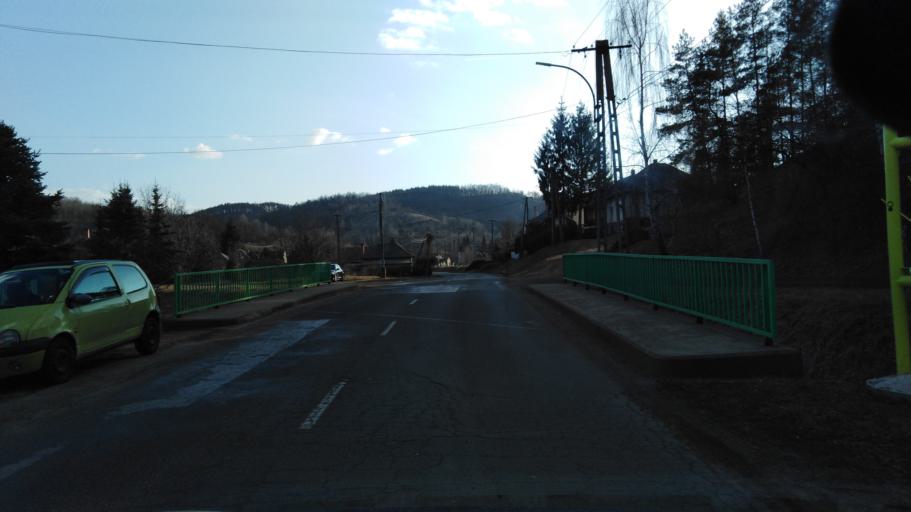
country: HU
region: Nograd
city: Somoskoujfalu
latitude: 48.1167
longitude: 19.8648
